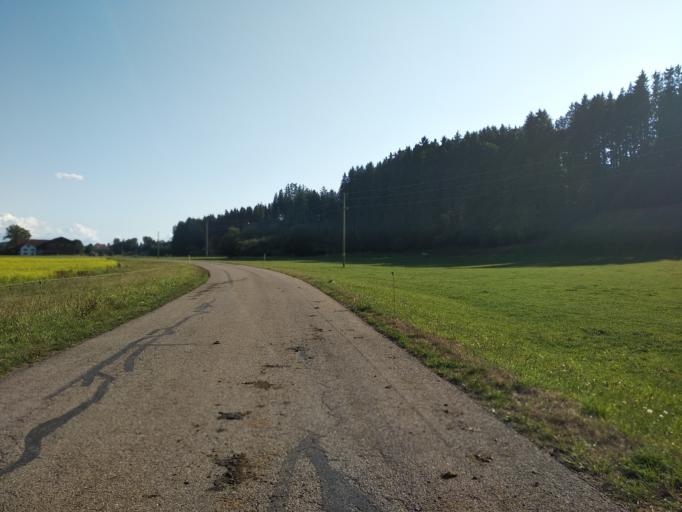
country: DE
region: Bavaria
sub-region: Swabia
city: Lautrach
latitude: 47.8785
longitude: 10.1185
